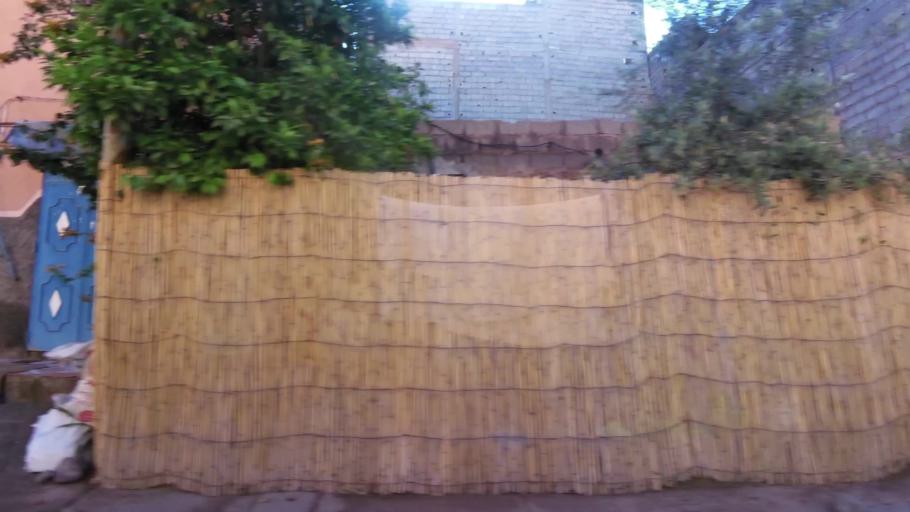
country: MA
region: Marrakech-Tensift-Al Haouz
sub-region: Marrakech
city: Marrakesh
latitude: 31.5944
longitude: -8.0248
